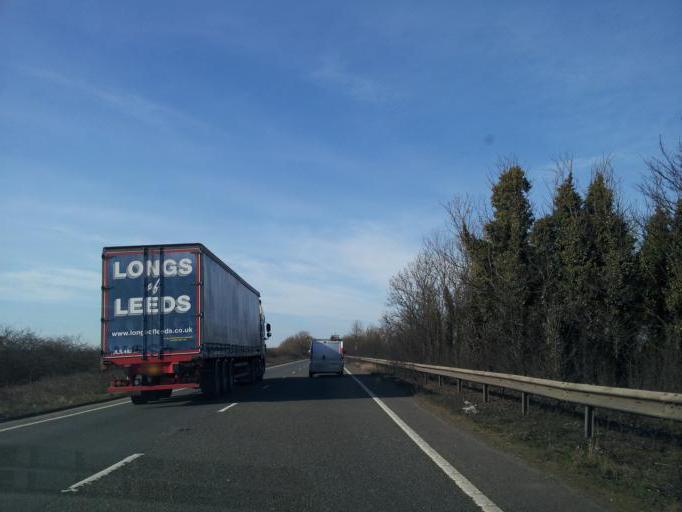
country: GB
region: England
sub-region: District of Rutland
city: Tickencote
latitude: 52.6815
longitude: -0.5451
